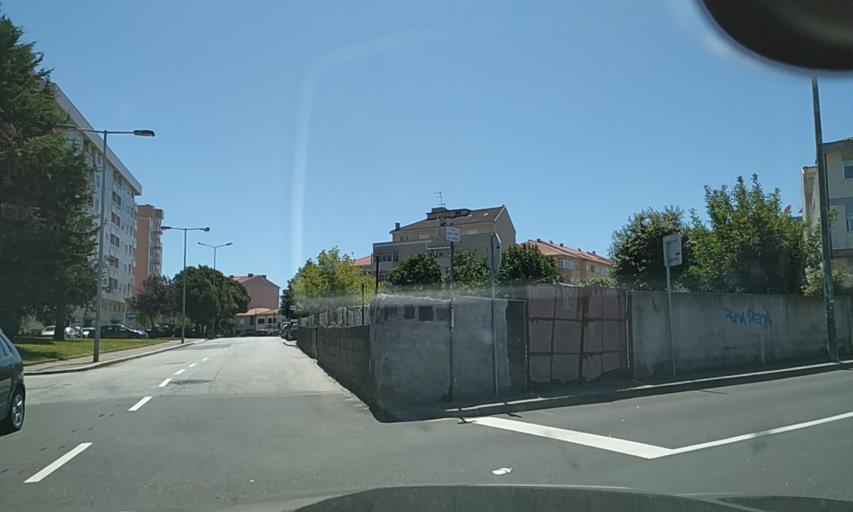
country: PT
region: Porto
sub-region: Vila Nova de Gaia
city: Canidelo
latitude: 41.1310
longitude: -8.6447
